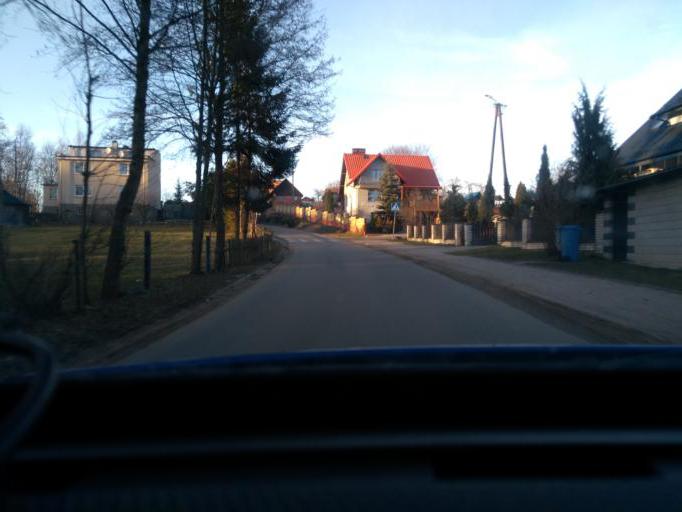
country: PL
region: Pomeranian Voivodeship
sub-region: Powiat kartuski
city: Przodkowo
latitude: 54.3750
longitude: 18.2648
